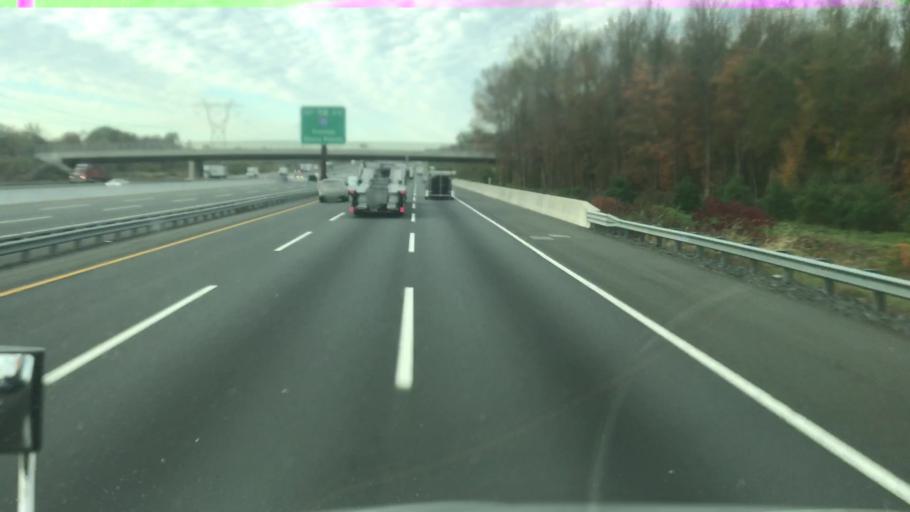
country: US
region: New Jersey
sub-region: Monmouth County
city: Shrewsbury
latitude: 40.2221
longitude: -74.5600
